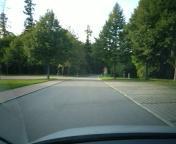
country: DE
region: Baden-Wuerttemberg
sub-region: Karlsruhe Region
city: Hofen an der Enz
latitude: 48.8241
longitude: 8.5572
